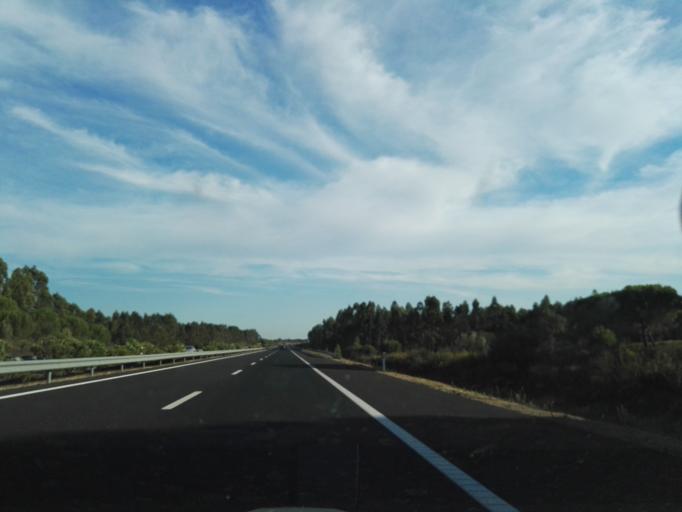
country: PT
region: Santarem
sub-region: Benavente
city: Poceirao
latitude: 38.7969
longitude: -8.6947
